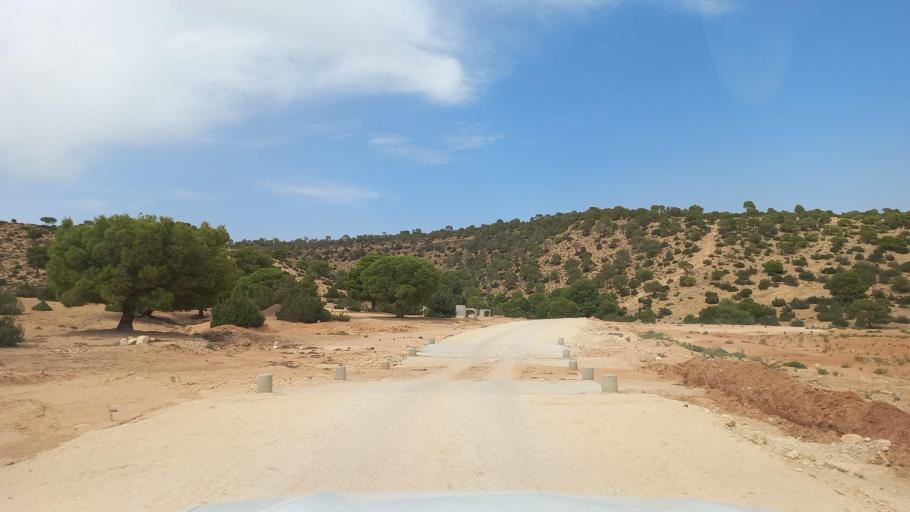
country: TN
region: Al Qasrayn
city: Kasserine
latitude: 35.3729
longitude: 8.8879
